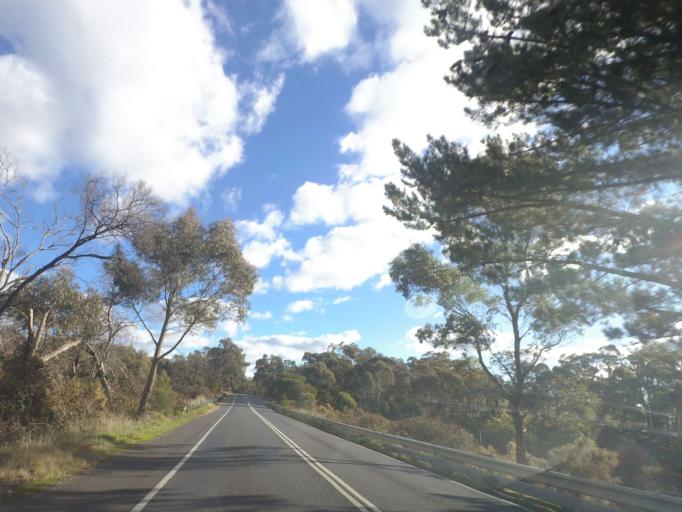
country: AU
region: Victoria
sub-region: Mount Alexander
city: Castlemaine
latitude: -37.1050
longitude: 144.3101
